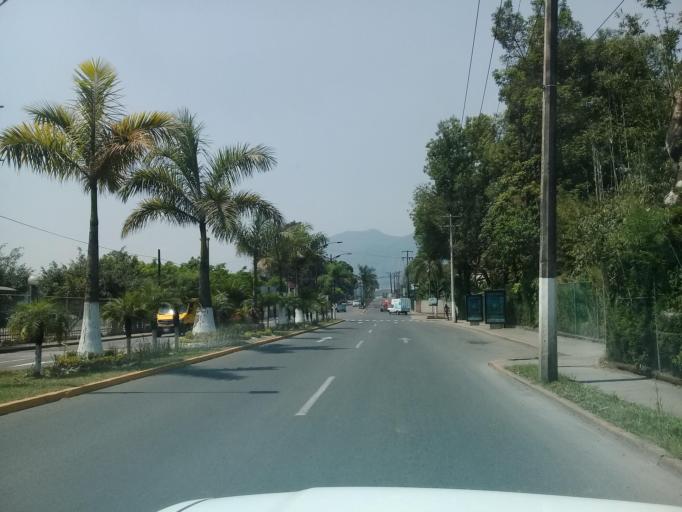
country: MX
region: Veracruz
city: Ixtac Zoquitlan
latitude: 18.8623
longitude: -97.0478
